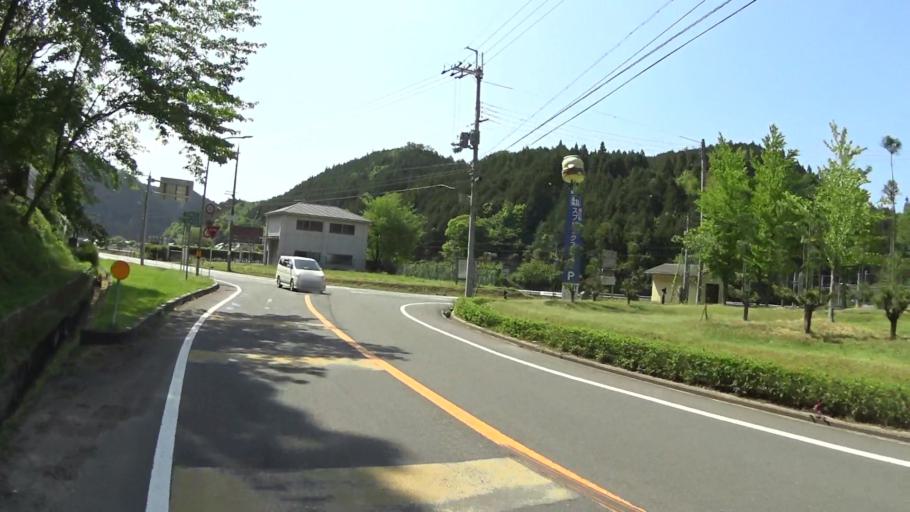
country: JP
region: Kyoto
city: Kameoka
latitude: 35.1523
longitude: 135.5076
